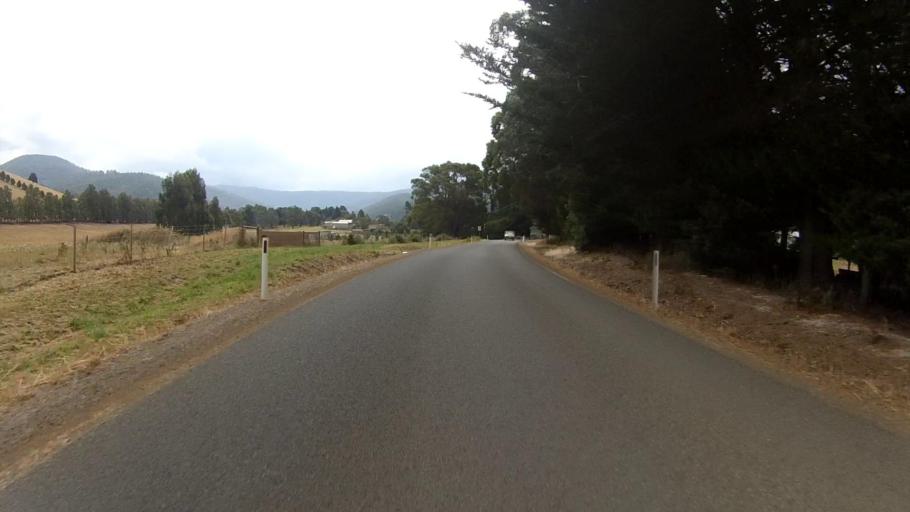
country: AU
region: Tasmania
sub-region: Huon Valley
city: Huonville
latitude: -42.9845
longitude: 147.0578
